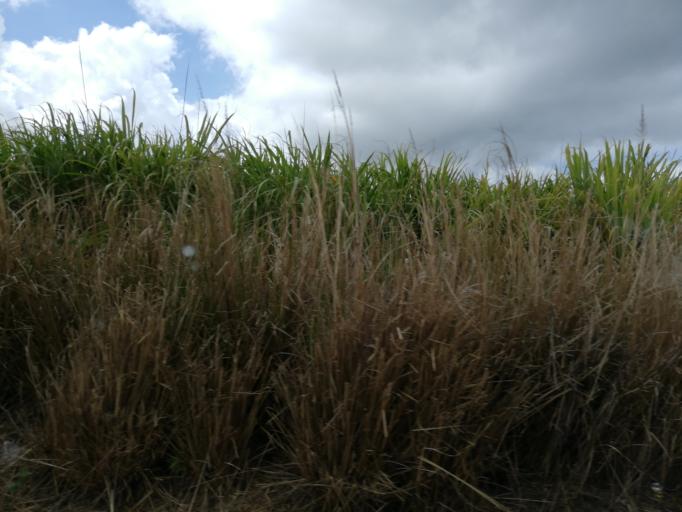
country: MU
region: Pamplemousses
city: Arsenal
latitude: -20.0913
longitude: 57.5436
